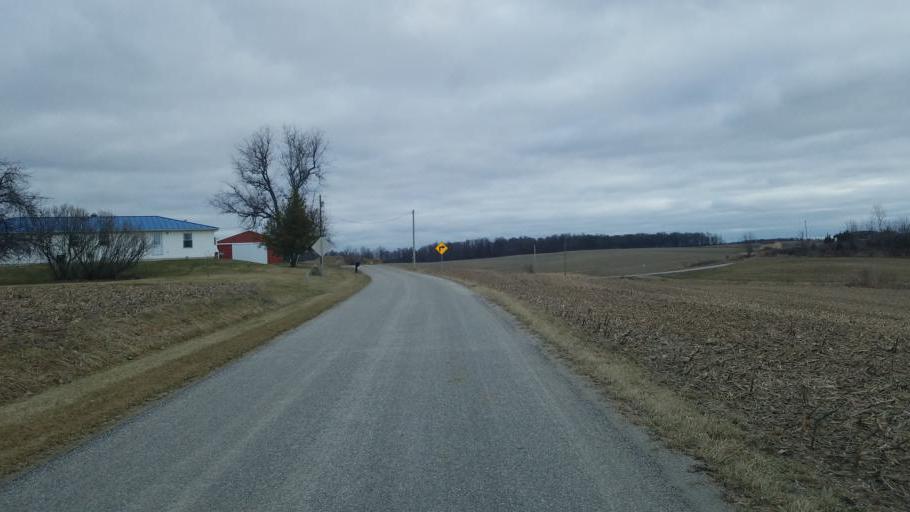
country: US
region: Ohio
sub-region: Morrow County
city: Mount Gilead
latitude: 40.5783
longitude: -82.6930
